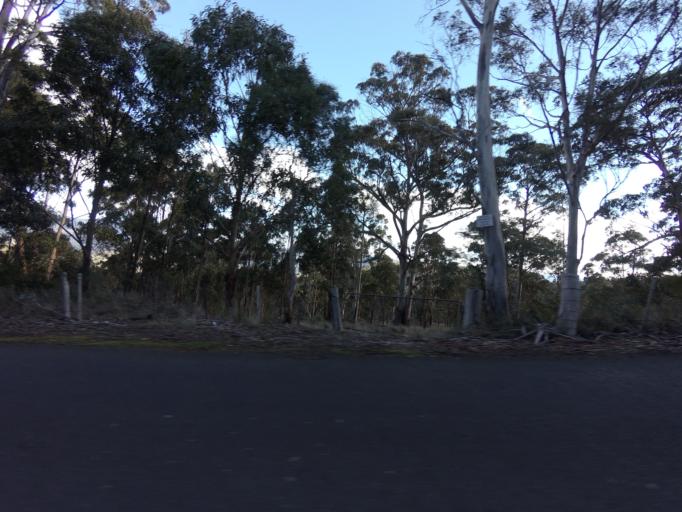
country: AU
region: Tasmania
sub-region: Derwent Valley
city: New Norfolk
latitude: -42.7293
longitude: 147.0317
